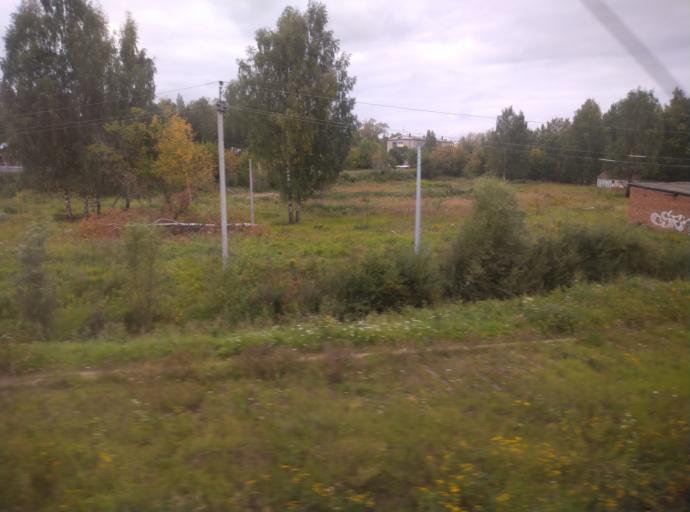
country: RU
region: Kostroma
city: Nerekhta
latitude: 57.4660
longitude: 40.5589
